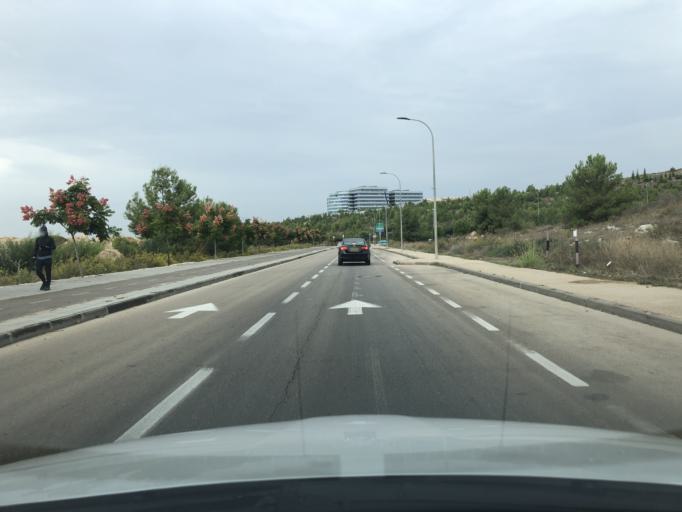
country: PS
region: West Bank
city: Al Midyah
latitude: 31.9196
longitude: 34.9961
